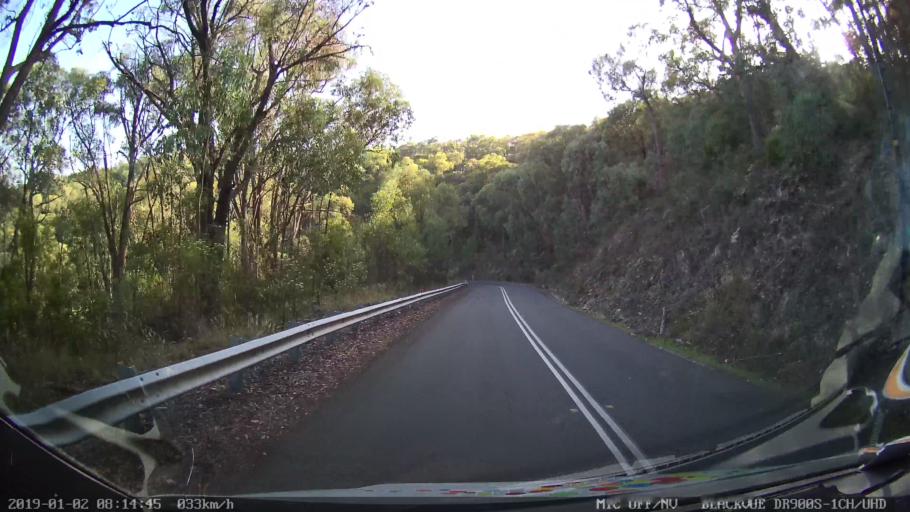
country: AU
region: New South Wales
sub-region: Tumut Shire
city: Tumut
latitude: -35.5850
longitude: 148.3395
